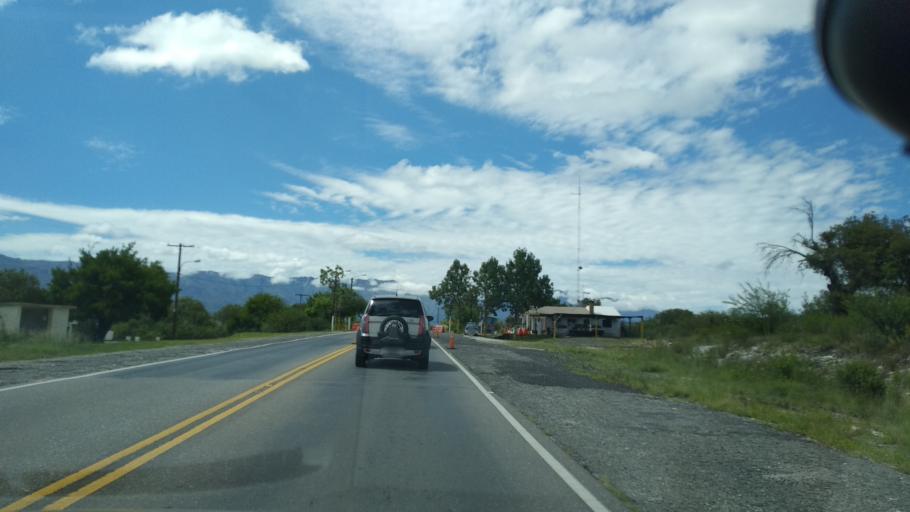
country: AR
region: Cordoba
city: Mina Clavero
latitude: -31.7504
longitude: -64.9781
